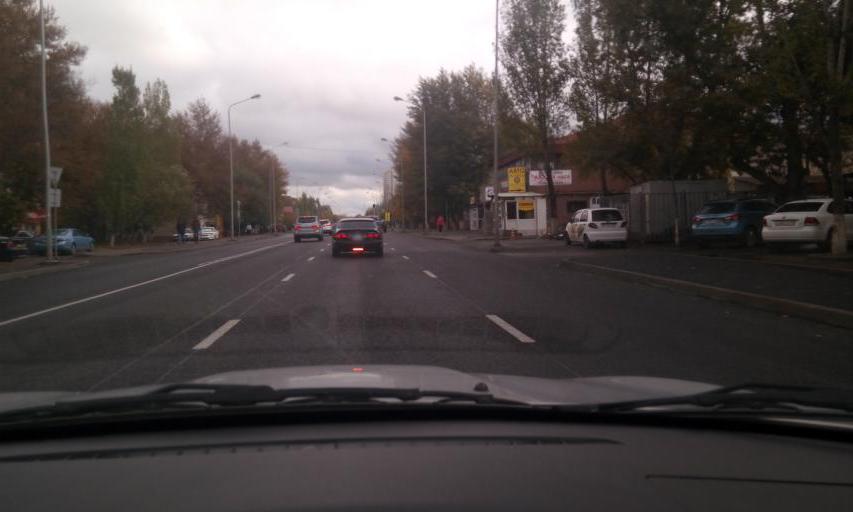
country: KZ
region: Astana Qalasy
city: Astana
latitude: 51.1688
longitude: 71.4546
